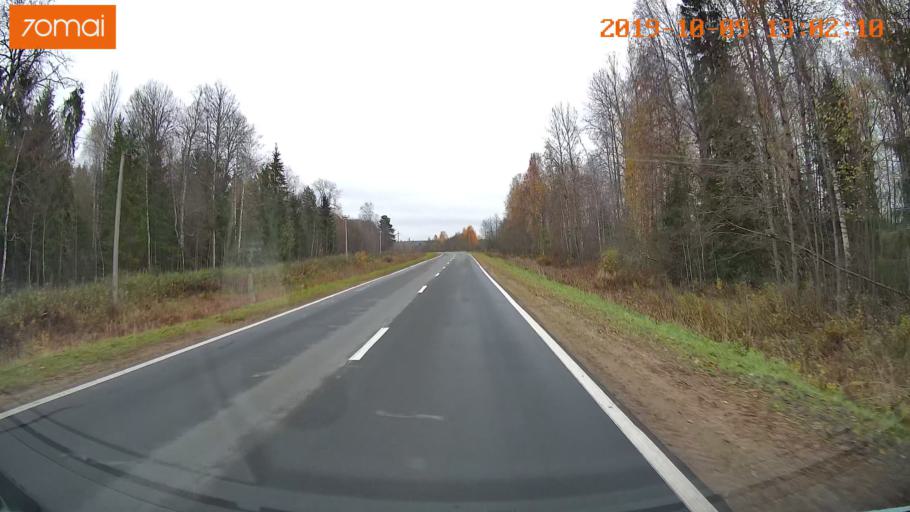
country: RU
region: Jaroslavl
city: Prechistoye
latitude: 58.3634
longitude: 40.4960
